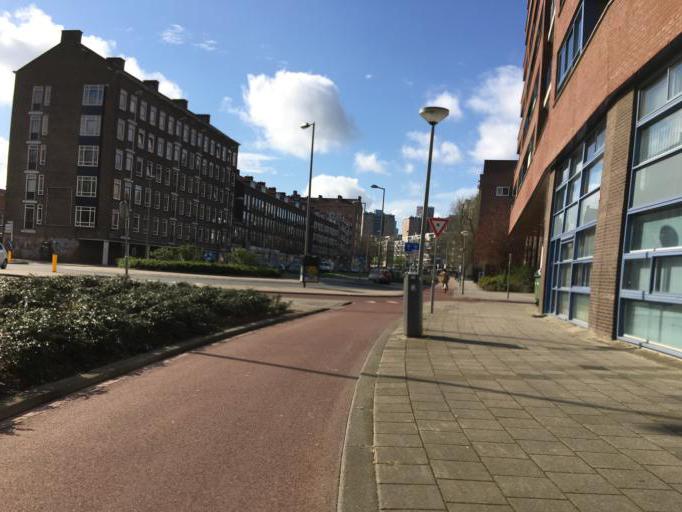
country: NL
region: South Holland
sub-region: Gemeente Rotterdam
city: Rotterdam
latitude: 51.9264
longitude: 4.4889
